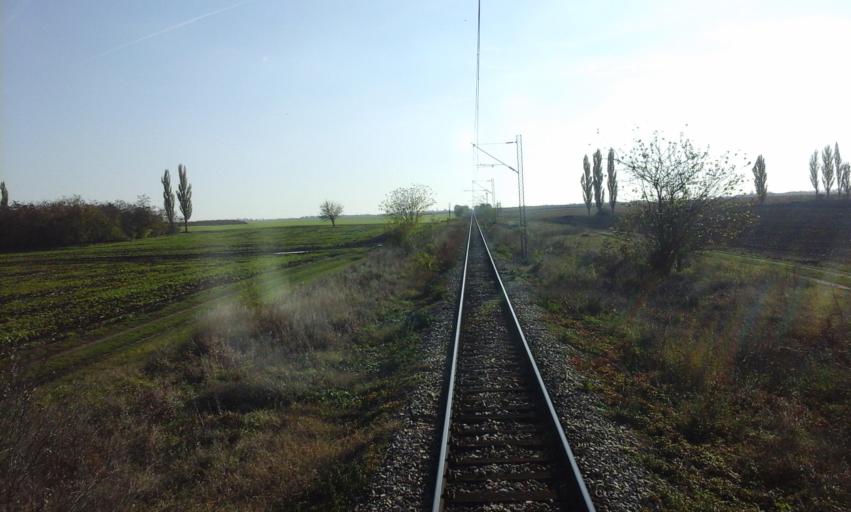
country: RS
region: Autonomna Pokrajina Vojvodina
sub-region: Severnobacki Okrug
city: Backa Topola
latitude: 45.7783
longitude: 19.6479
